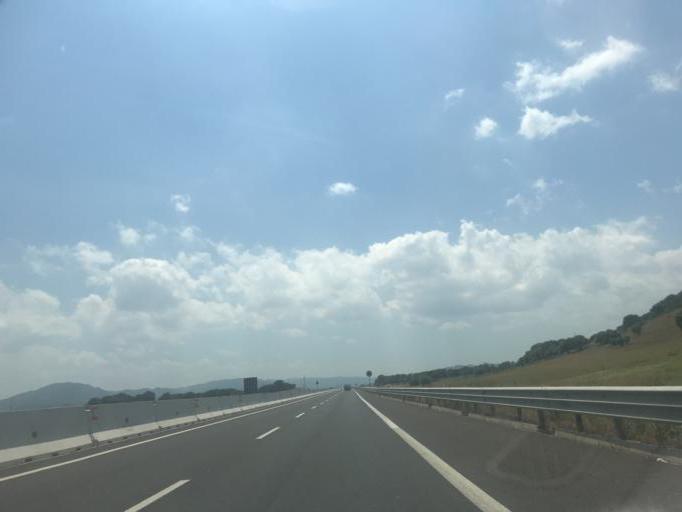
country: IT
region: Sardinia
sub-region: Provincia di Olbia-Tempio
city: Olbia
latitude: 40.8902
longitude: 9.4817
